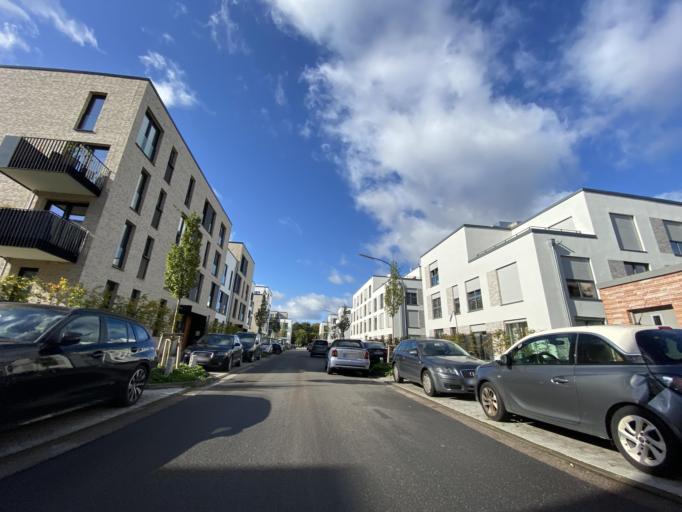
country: DE
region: Hamburg
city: Hamburg-Nord
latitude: 53.5957
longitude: 9.9728
